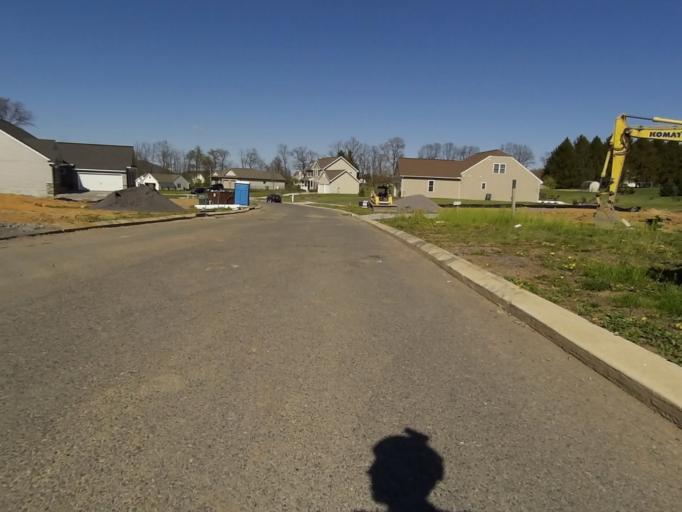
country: US
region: Pennsylvania
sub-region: Centre County
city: Houserville
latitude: 40.8775
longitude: -77.8300
